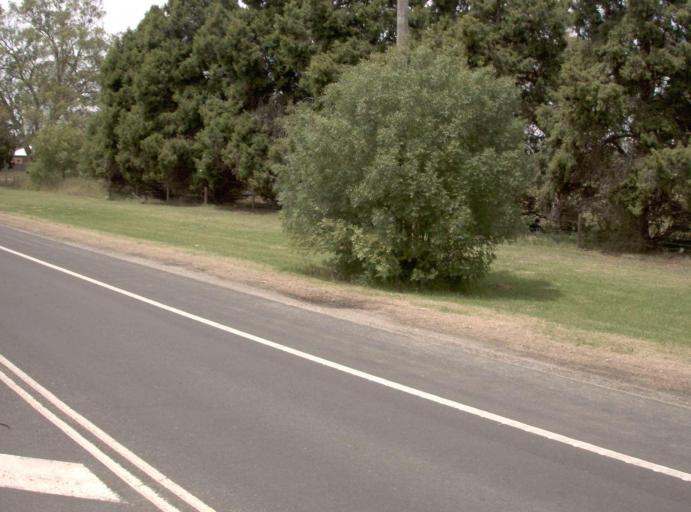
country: AU
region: Victoria
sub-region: Wellington
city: Sale
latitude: -38.0860
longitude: 147.0586
